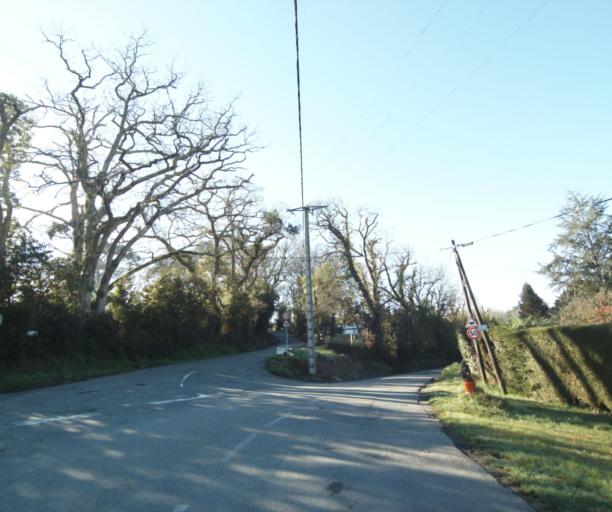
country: FR
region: Aquitaine
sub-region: Departement des Pyrenees-Atlantiques
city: Ciboure
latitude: 43.3707
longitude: -1.6704
